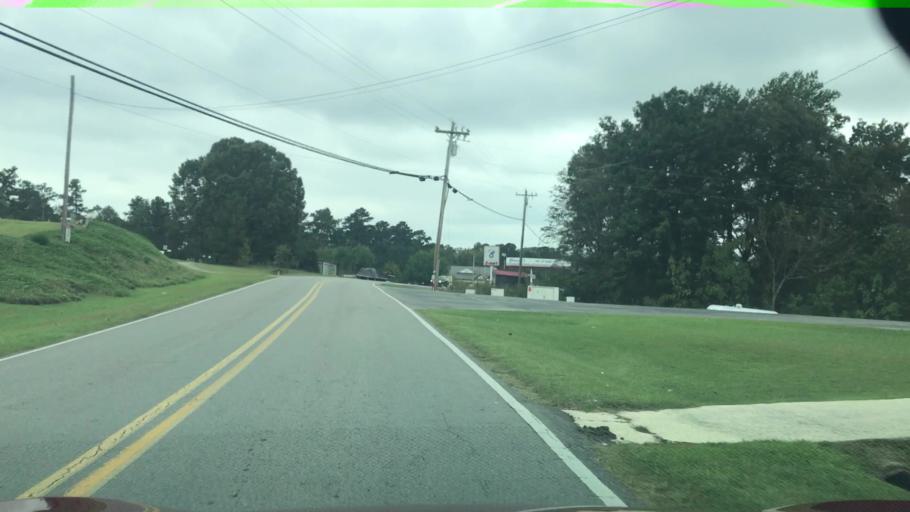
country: US
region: Alabama
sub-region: Cullman County
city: Good Hope
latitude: 34.0952
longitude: -87.0605
